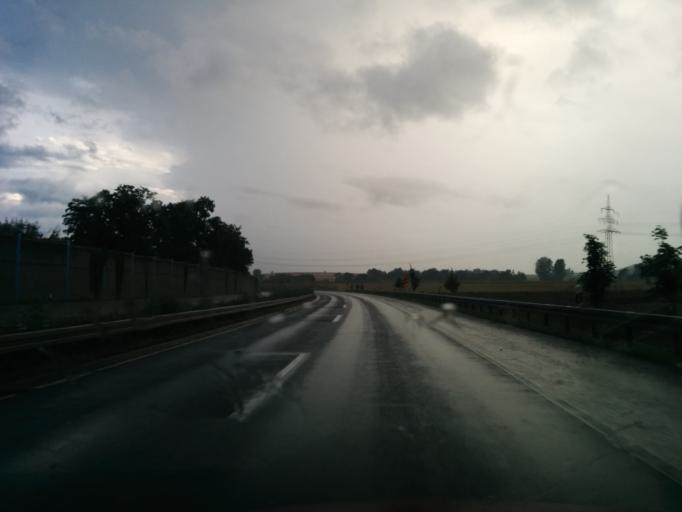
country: DE
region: Hesse
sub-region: Regierungsbezirk Giessen
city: Steeden
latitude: 50.4641
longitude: 8.1242
